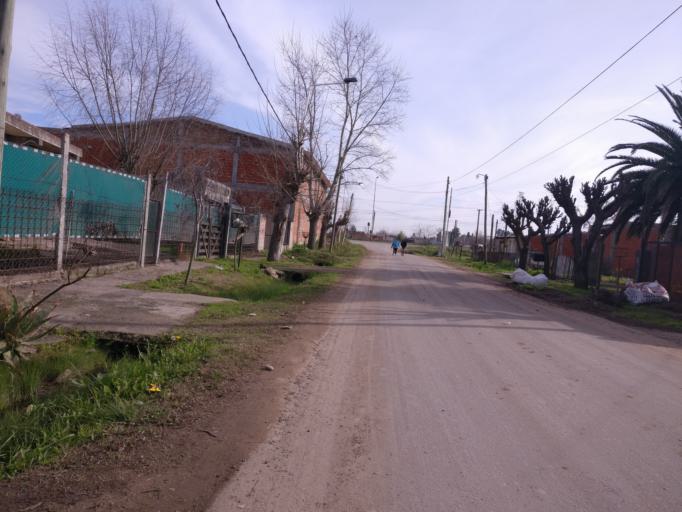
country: AR
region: Buenos Aires
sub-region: Partido de Ezeiza
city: Ezeiza
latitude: -34.9320
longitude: -58.6152
